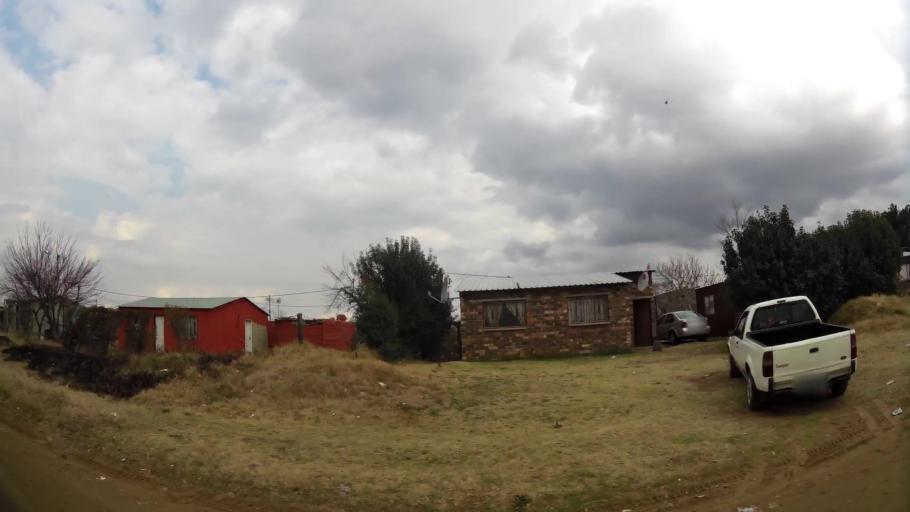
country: ZA
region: Orange Free State
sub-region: Fezile Dabi District Municipality
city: Sasolburg
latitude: -26.8666
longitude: 27.8702
